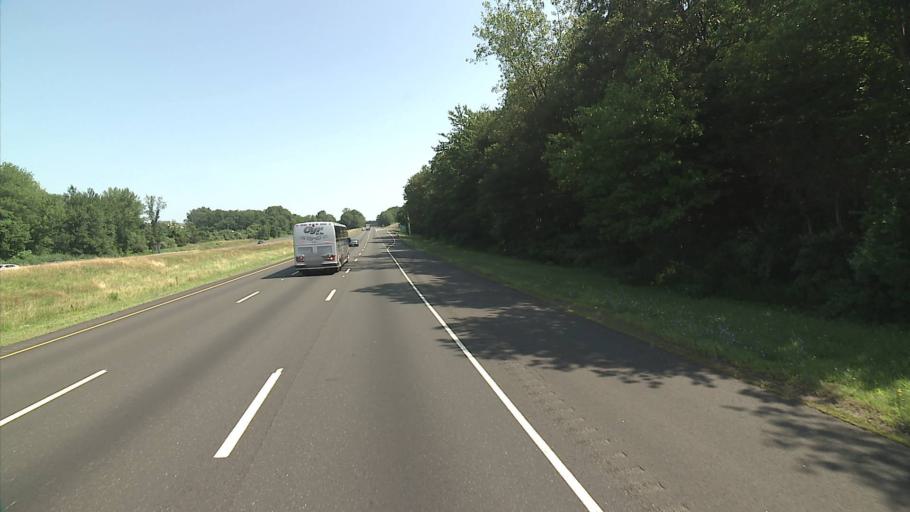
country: US
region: Connecticut
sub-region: New Haven County
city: Wallingford Center
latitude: 41.4739
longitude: -72.7720
